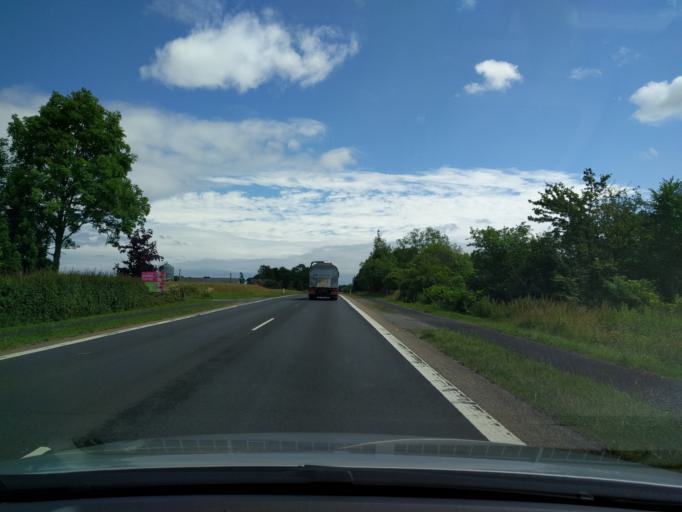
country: DK
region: South Denmark
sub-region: Nyborg Kommune
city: Ullerslev
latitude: 55.3624
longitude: 10.6204
